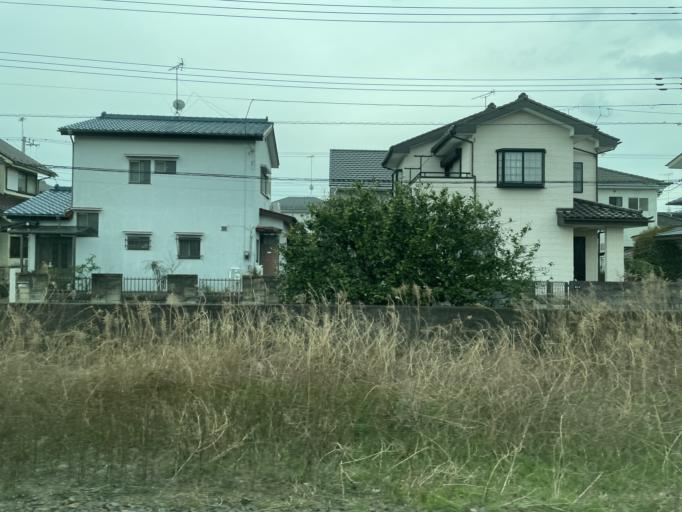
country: JP
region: Saitama
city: Sugito
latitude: 36.0298
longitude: 139.7174
